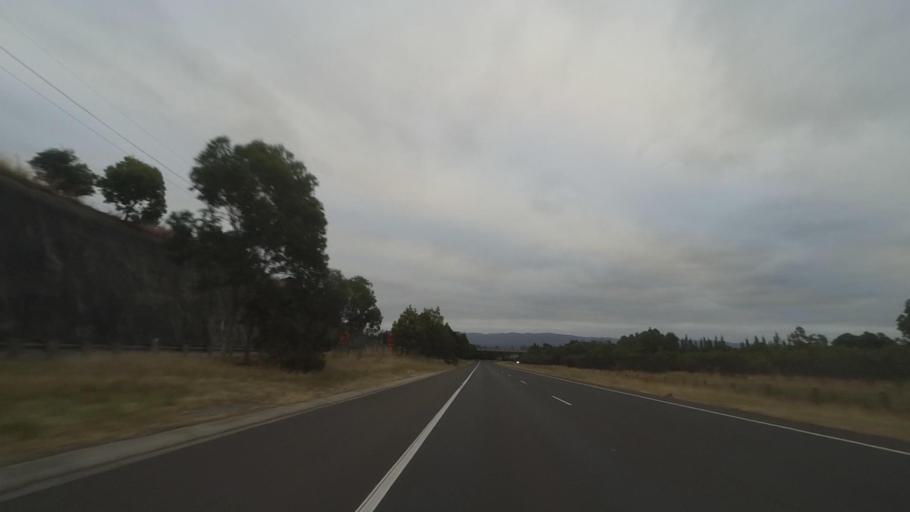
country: AU
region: New South Wales
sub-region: Shellharbour
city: Croom
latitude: -34.5748
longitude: 150.8254
